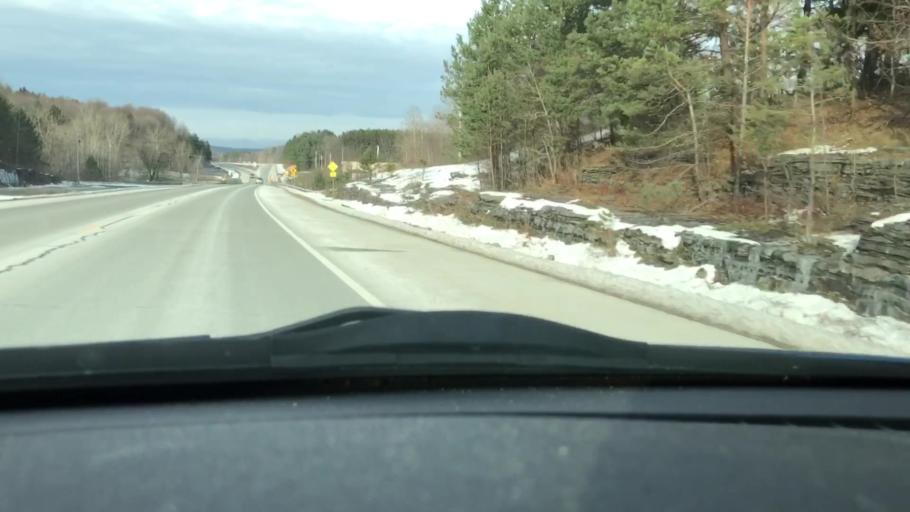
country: US
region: New York
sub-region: Oneida County
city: Boonville
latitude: 43.5235
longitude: -75.3254
